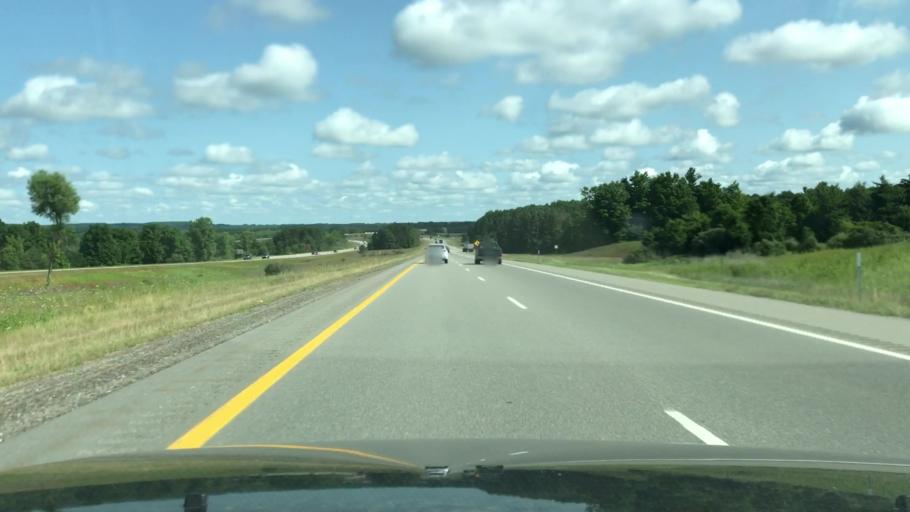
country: US
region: Michigan
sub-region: Mecosta County
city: Big Rapids
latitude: 43.5851
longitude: -85.4887
